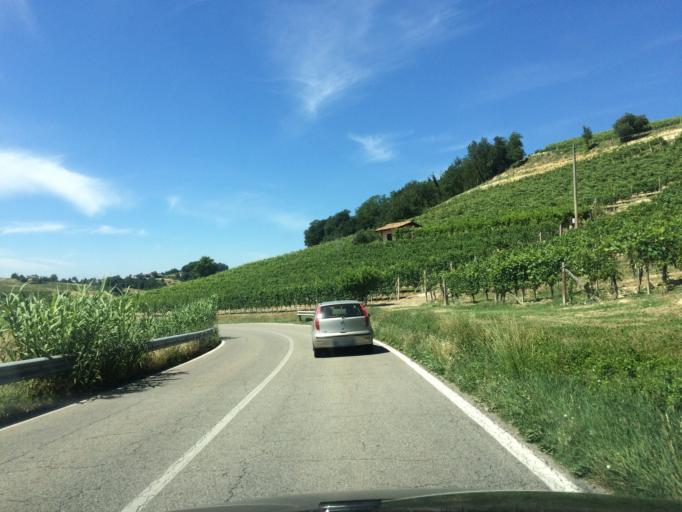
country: IT
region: Piedmont
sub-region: Provincia di Asti
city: Castel Boglione
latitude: 44.7501
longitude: 8.3740
